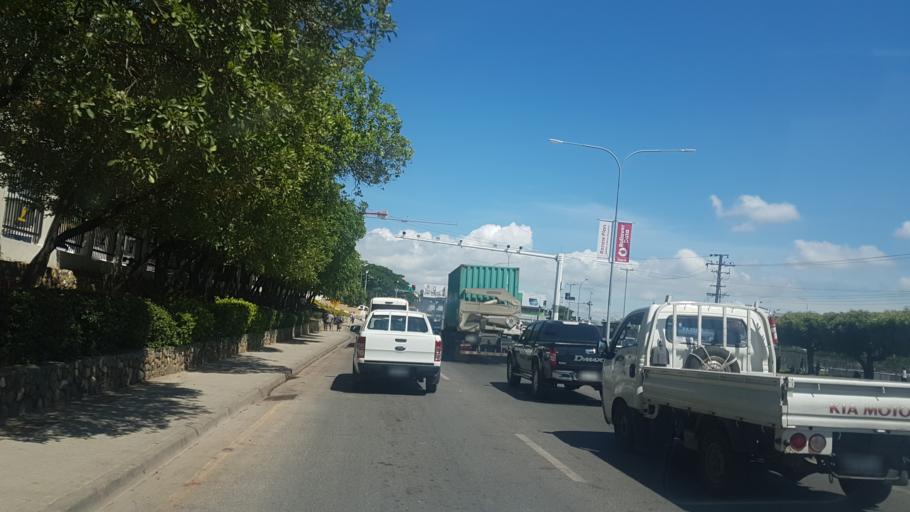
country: PG
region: National Capital
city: Port Moresby
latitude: -9.4412
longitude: 147.1810
